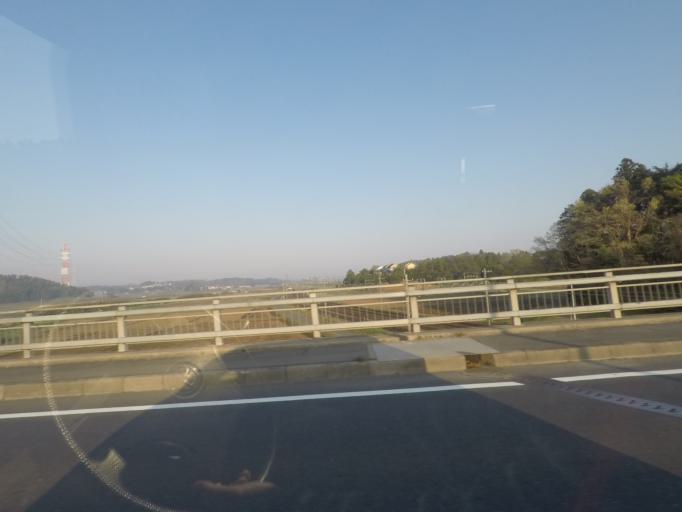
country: JP
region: Chiba
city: Shisui
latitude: 35.7062
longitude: 140.2514
